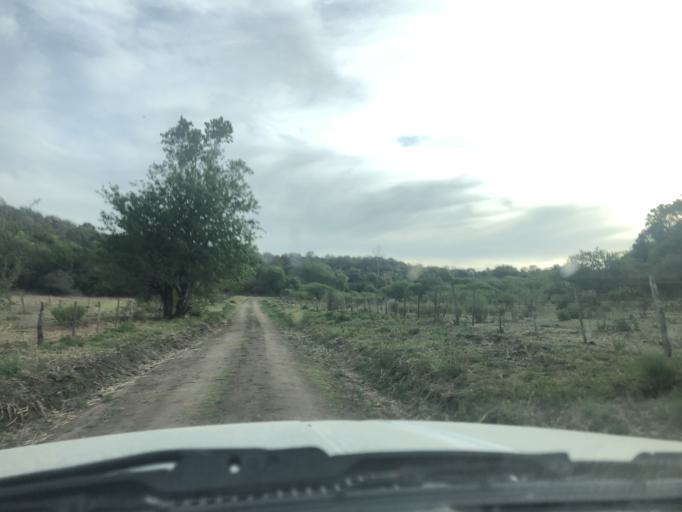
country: AR
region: Cordoba
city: La Granja
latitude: -31.0126
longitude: -64.2473
